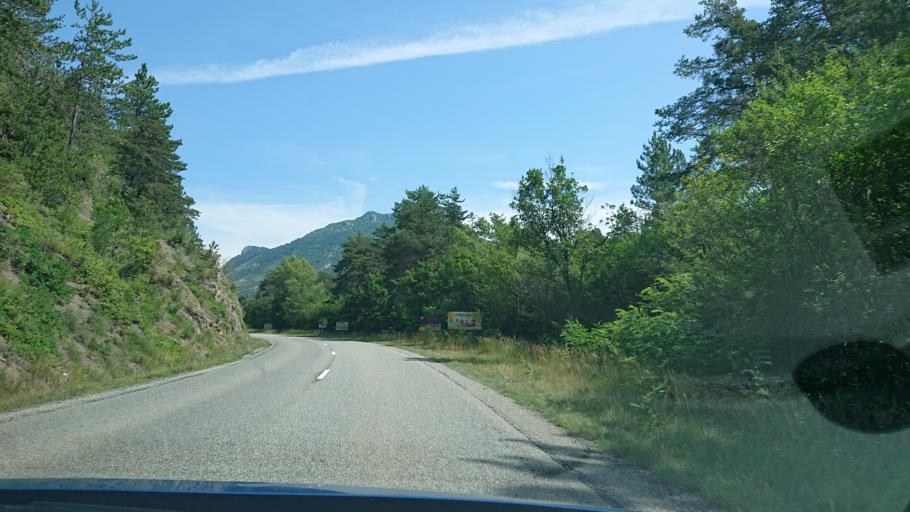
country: FR
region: Provence-Alpes-Cote d'Azur
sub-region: Departement des Alpes-de-Haute-Provence
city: Sisteron
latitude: 44.3064
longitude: 6.0349
